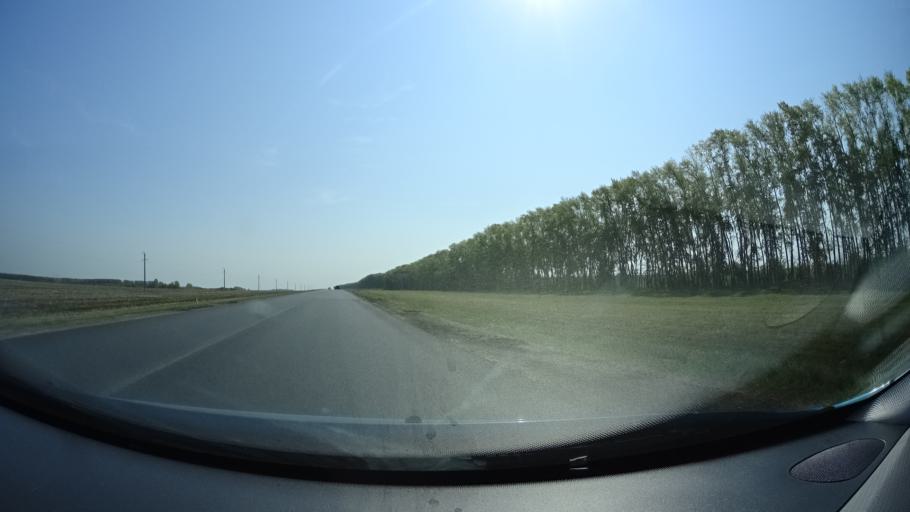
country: RU
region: Bashkortostan
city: Karmaskaly
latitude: 54.4117
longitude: 56.0646
